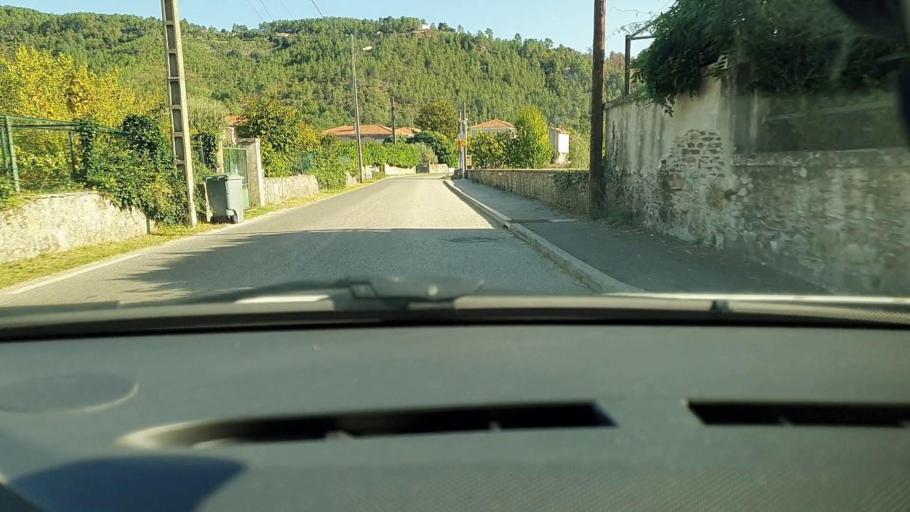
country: FR
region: Languedoc-Roussillon
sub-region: Departement du Gard
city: Besseges
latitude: 44.2975
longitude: 4.0784
